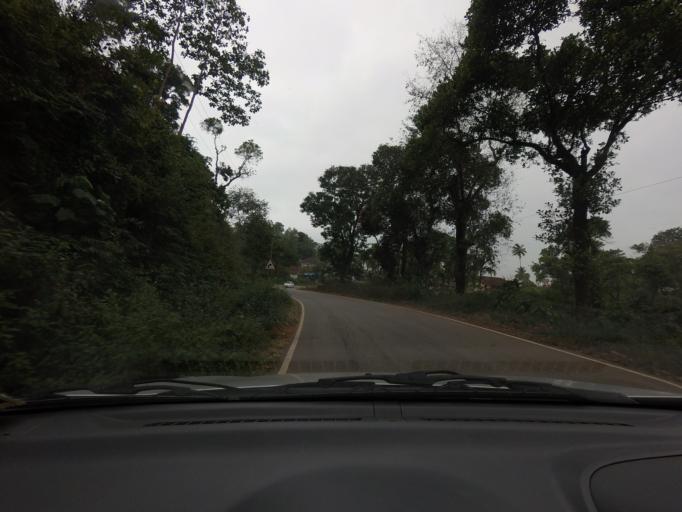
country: IN
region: Karnataka
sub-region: Hassan
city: Sakleshpur
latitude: 12.9309
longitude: 75.7637
